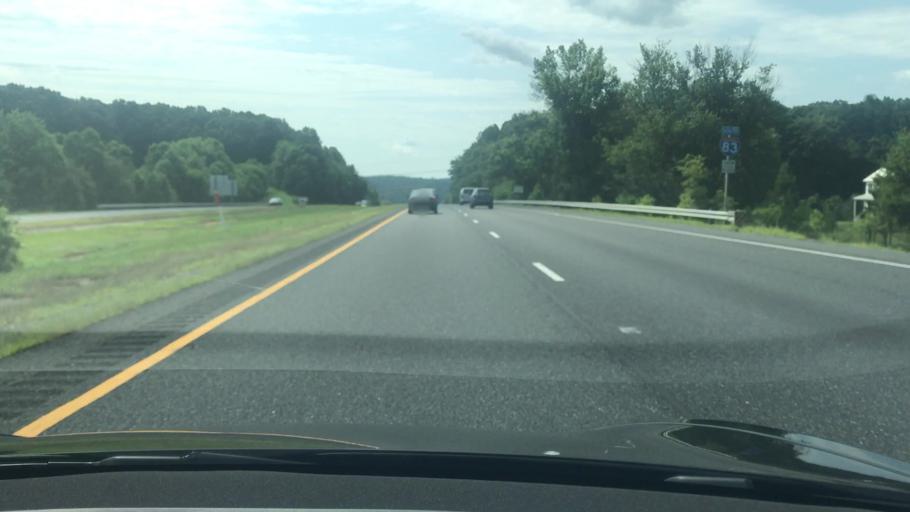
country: US
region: Pennsylvania
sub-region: York County
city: New Freedom
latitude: 39.6277
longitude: -76.6701
